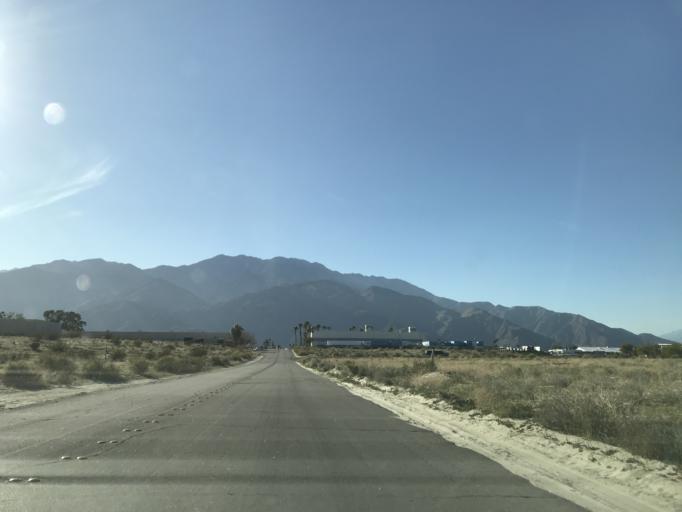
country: US
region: California
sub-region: Riverside County
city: Cathedral City
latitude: 33.8122
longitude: -116.4889
